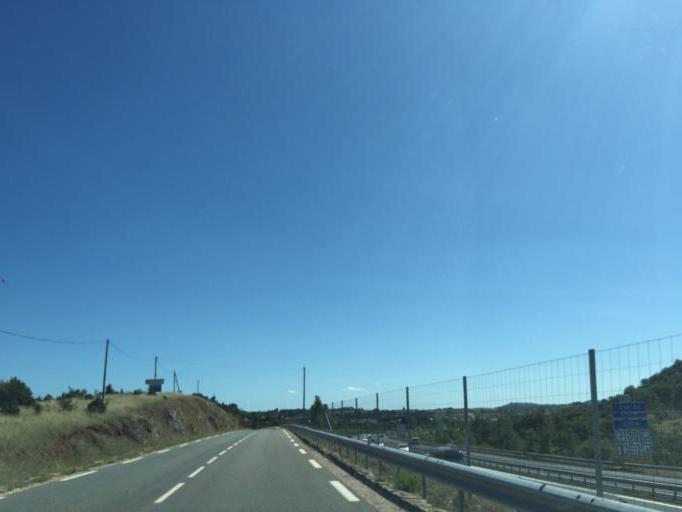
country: FR
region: Languedoc-Roussillon
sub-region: Departement de l'Herault
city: Lodeve
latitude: 43.8777
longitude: 3.3123
